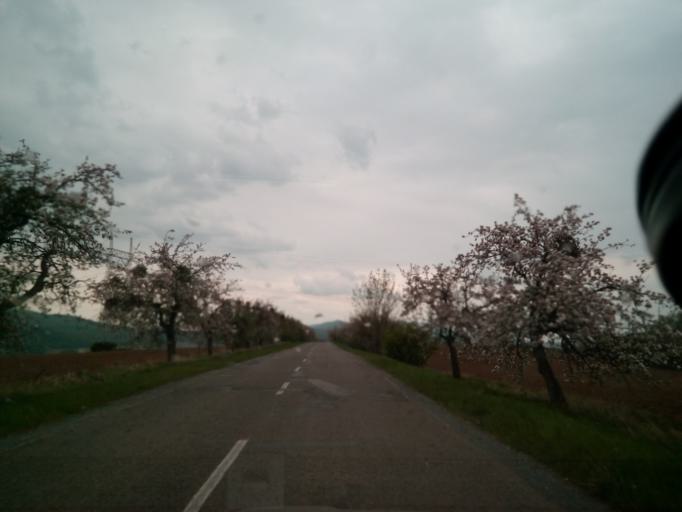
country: SK
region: Kosicky
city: Secovce
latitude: 48.7590
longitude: 21.4653
